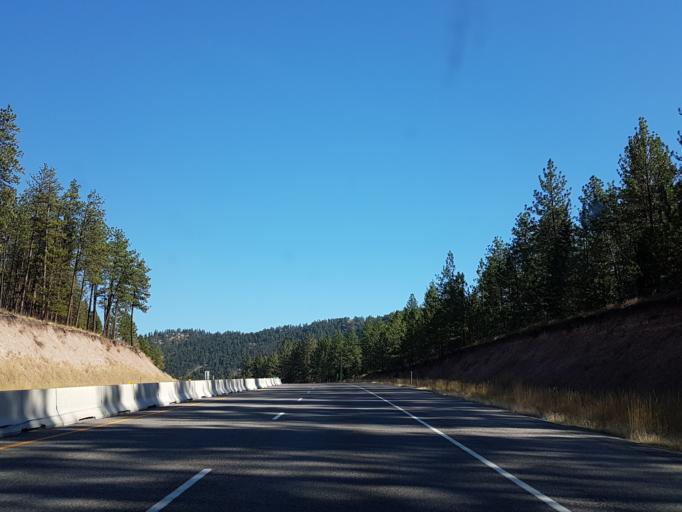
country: US
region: Montana
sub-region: Missoula County
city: Frenchtown
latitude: 47.0199
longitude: -114.3774
